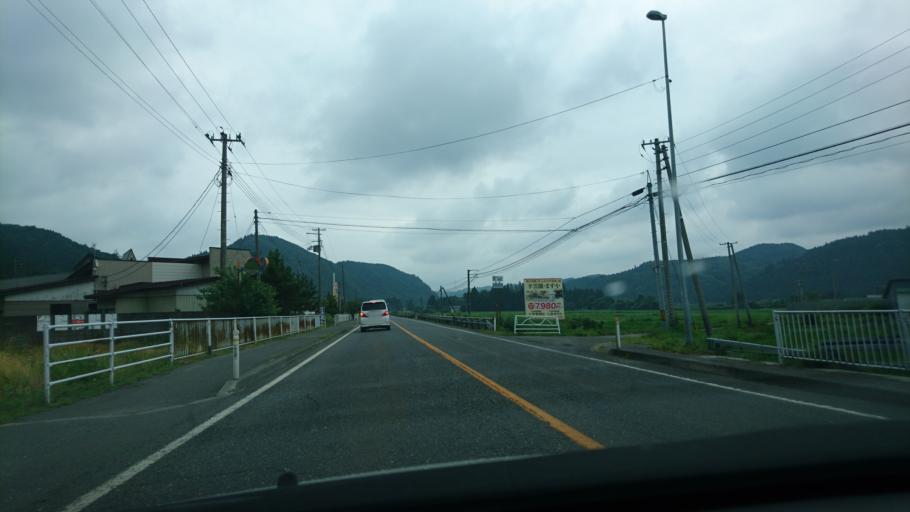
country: JP
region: Miyagi
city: Furukawa
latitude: 38.7305
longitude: 140.7927
